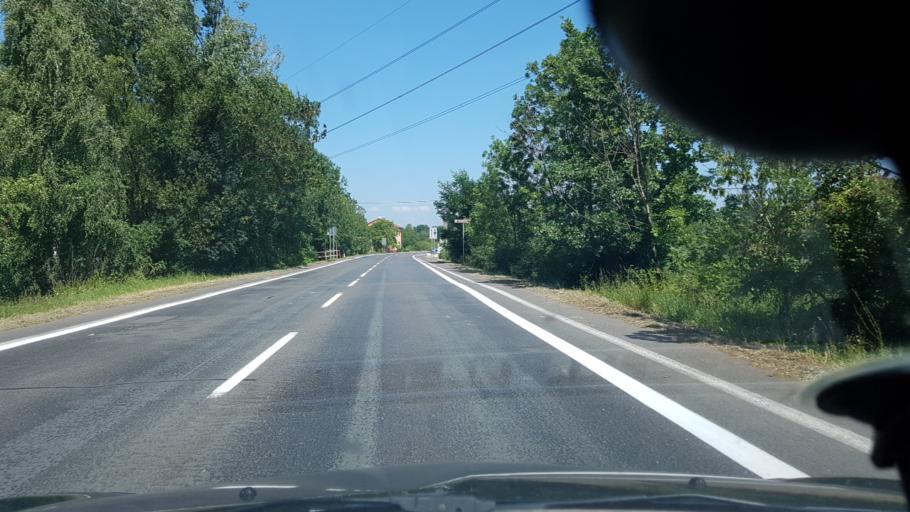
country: CZ
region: Moravskoslezsky
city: Stary Bohumin
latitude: 49.9013
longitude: 18.3355
